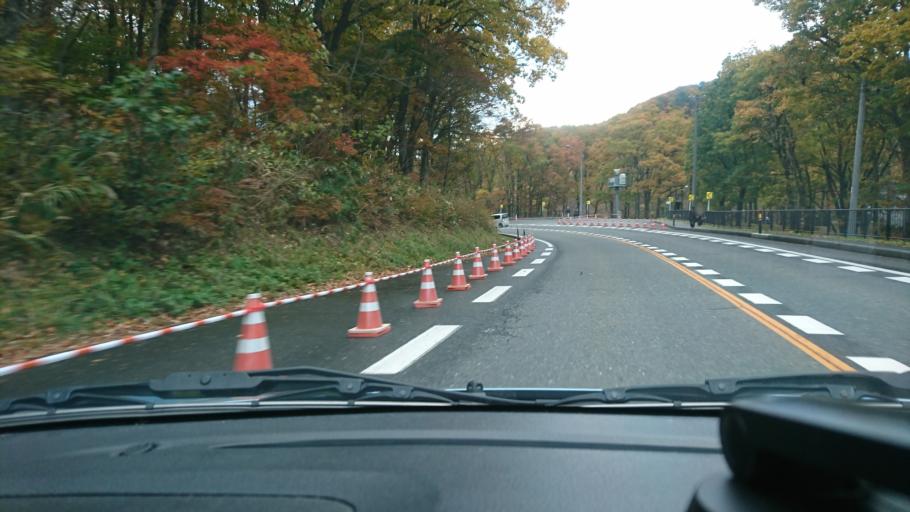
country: JP
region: Miyagi
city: Furukawa
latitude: 38.7286
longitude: 140.6885
